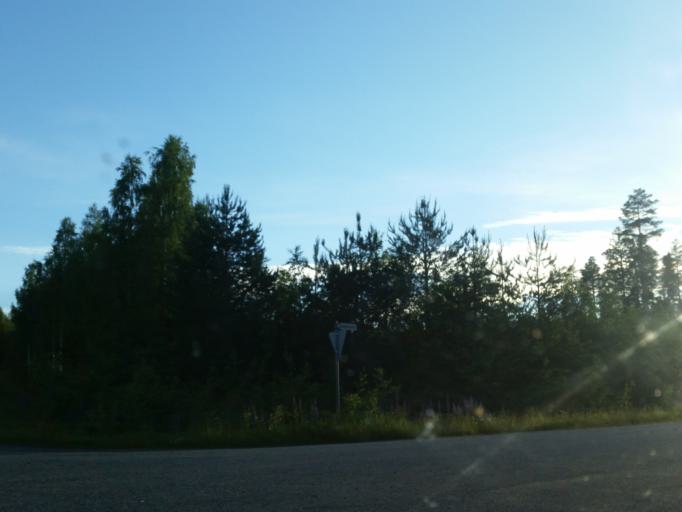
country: FI
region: Northern Savo
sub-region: Sisae-Savo
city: Tervo
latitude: 63.0281
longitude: 26.6919
